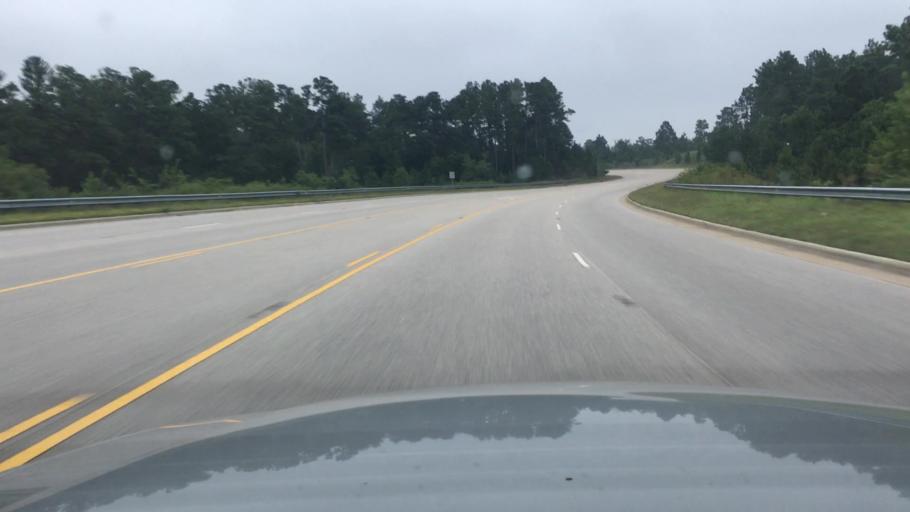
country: US
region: North Carolina
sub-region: Cumberland County
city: Fayetteville
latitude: 35.0156
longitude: -78.8893
